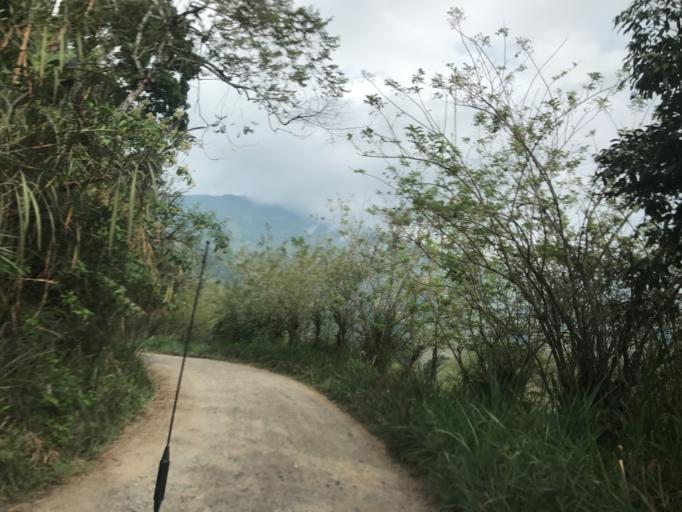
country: CO
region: Valle del Cauca
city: Obando
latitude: 4.5530
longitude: -75.8670
